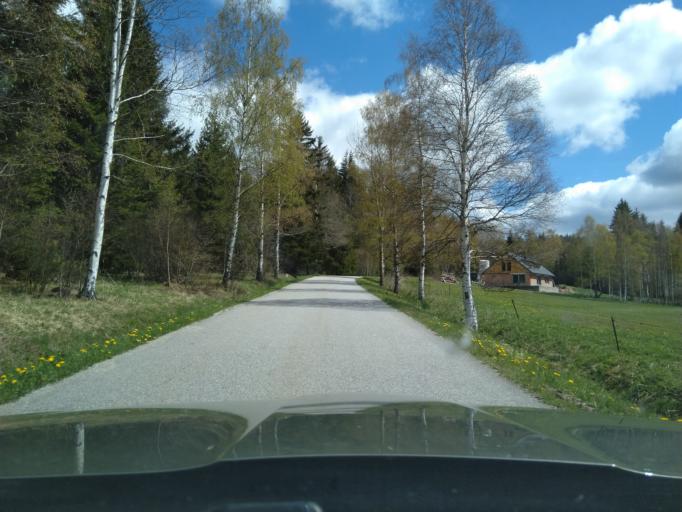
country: CZ
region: Jihocesky
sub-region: Okres Prachatice
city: Borova Lada
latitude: 48.9982
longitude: 13.6800
